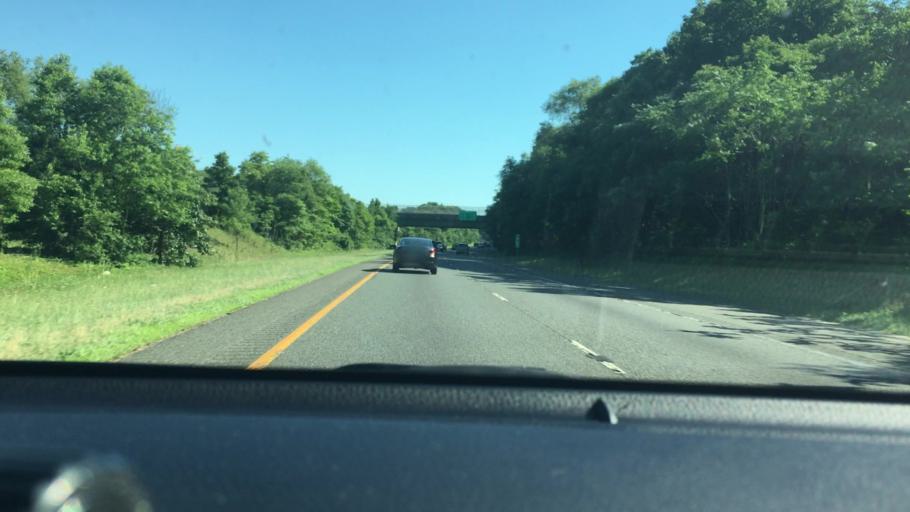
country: US
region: New Jersey
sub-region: Camden County
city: Glendora
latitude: 39.8233
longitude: -75.1050
